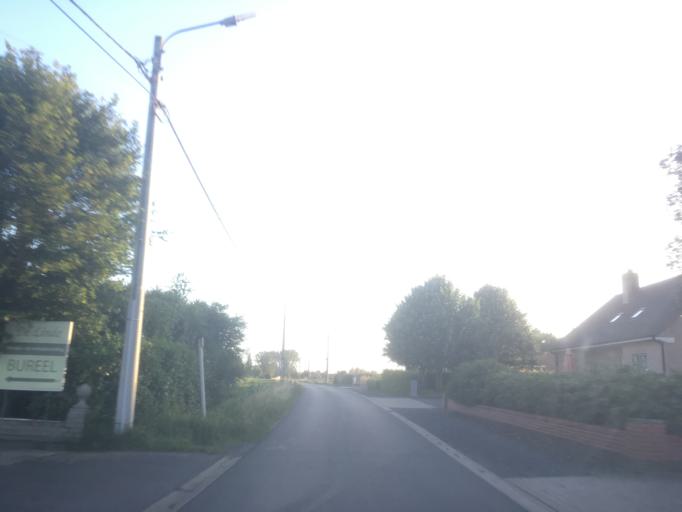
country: BE
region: Flanders
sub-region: Provincie West-Vlaanderen
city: Torhout
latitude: 51.0608
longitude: 3.0826
